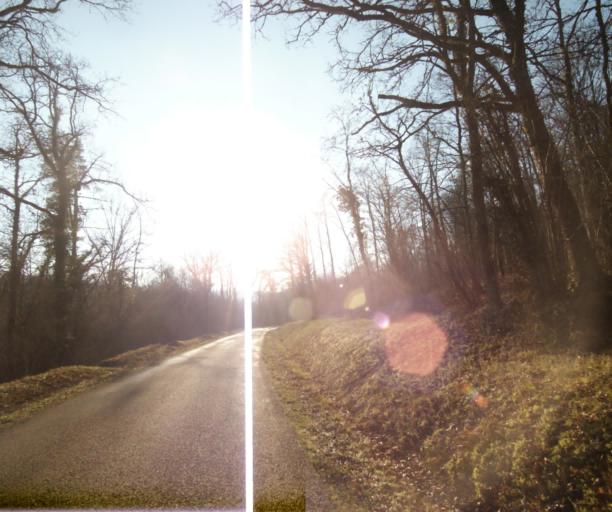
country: FR
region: Champagne-Ardenne
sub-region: Departement de la Haute-Marne
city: Chevillon
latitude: 48.5451
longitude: 5.1233
